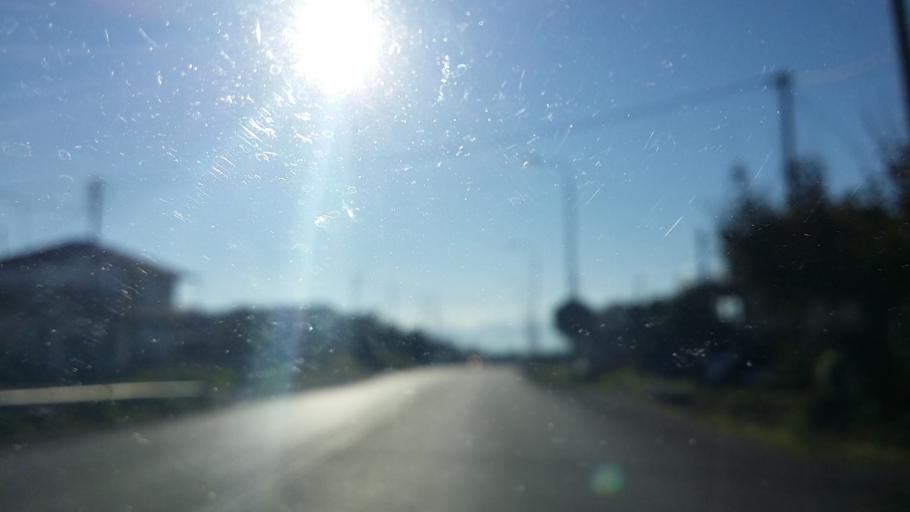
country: GR
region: West Greece
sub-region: Nomos Aitolias kai Akarnanias
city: Neapolis
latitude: 38.6642
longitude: 21.3662
